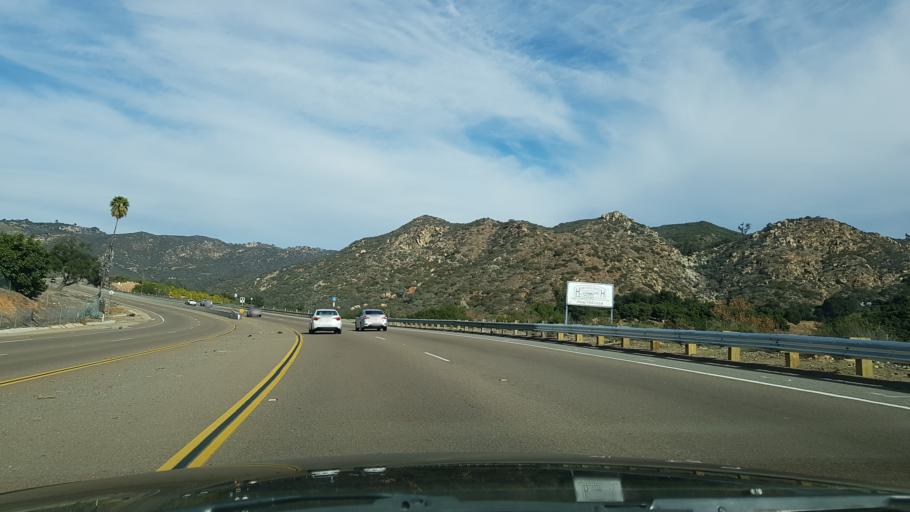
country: US
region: California
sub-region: San Diego County
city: Valley Center
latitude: 33.1694
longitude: -117.0268
